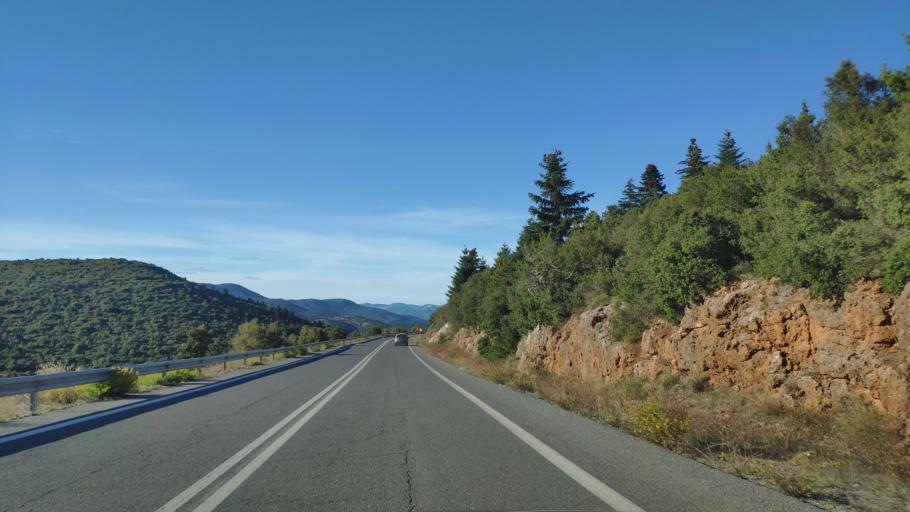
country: GR
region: Peloponnese
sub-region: Nomos Arkadias
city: Langadhia
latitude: 37.6990
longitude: 22.1988
